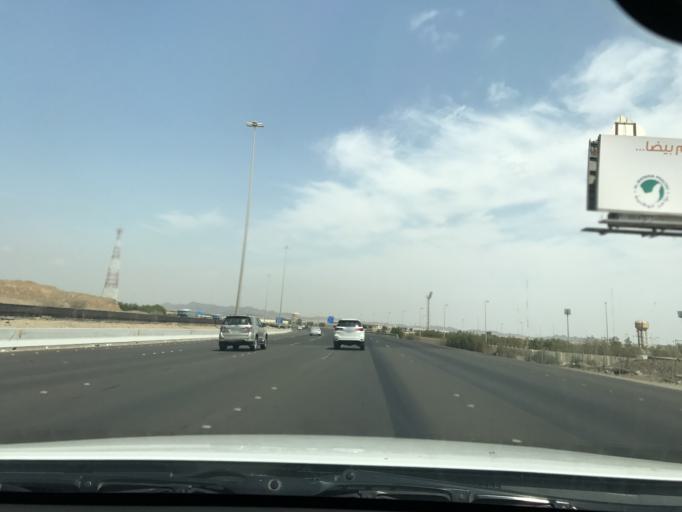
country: SA
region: Makkah
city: Jeddah
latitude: 21.3915
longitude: 39.4138
